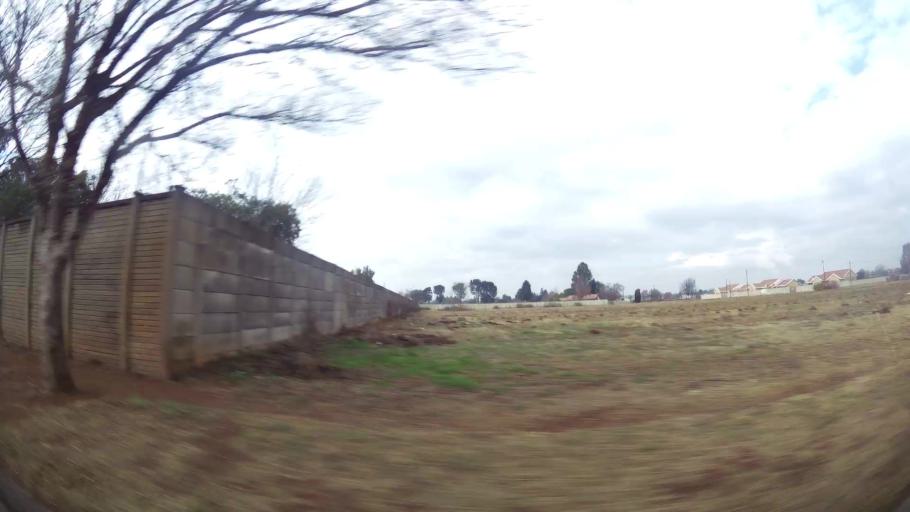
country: ZA
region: Gauteng
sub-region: Sedibeng District Municipality
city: Meyerton
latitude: -26.5935
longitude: 27.9955
